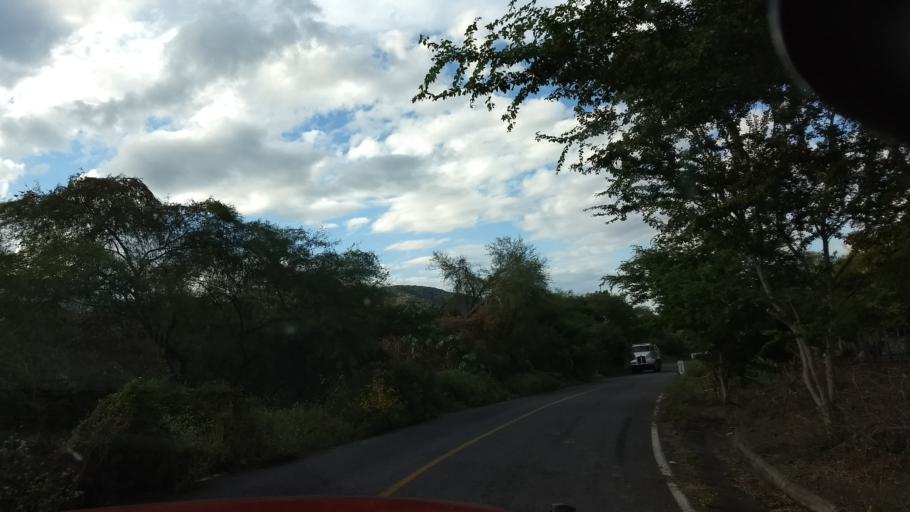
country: MX
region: Colima
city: Suchitlan
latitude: 19.4553
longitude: -103.8260
